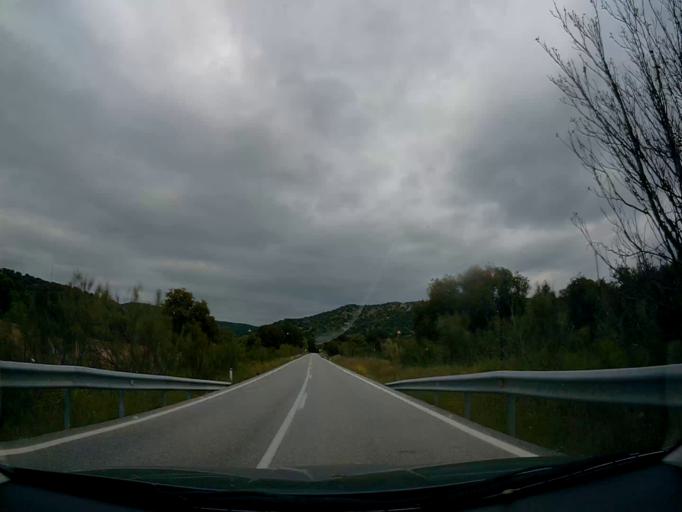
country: ES
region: Madrid
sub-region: Provincia de Madrid
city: Quijorna
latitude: 40.4271
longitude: -4.0925
